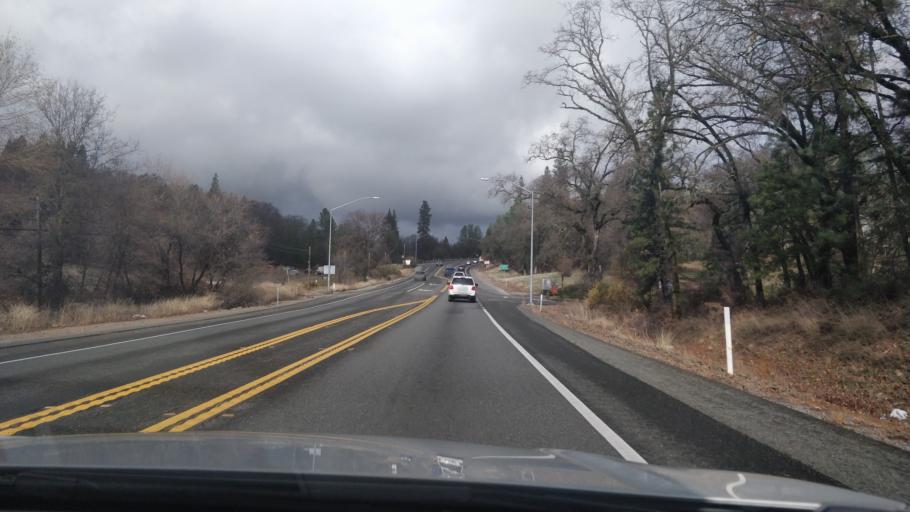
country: US
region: California
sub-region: Nevada County
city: Alta Sierra
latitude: 39.1238
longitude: -121.0781
